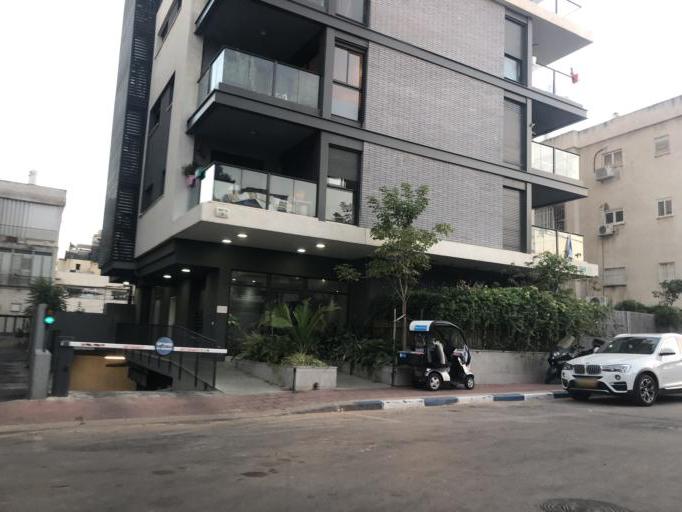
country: IL
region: Tel Aviv
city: Giv`atayim
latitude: 32.0643
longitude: 34.8261
